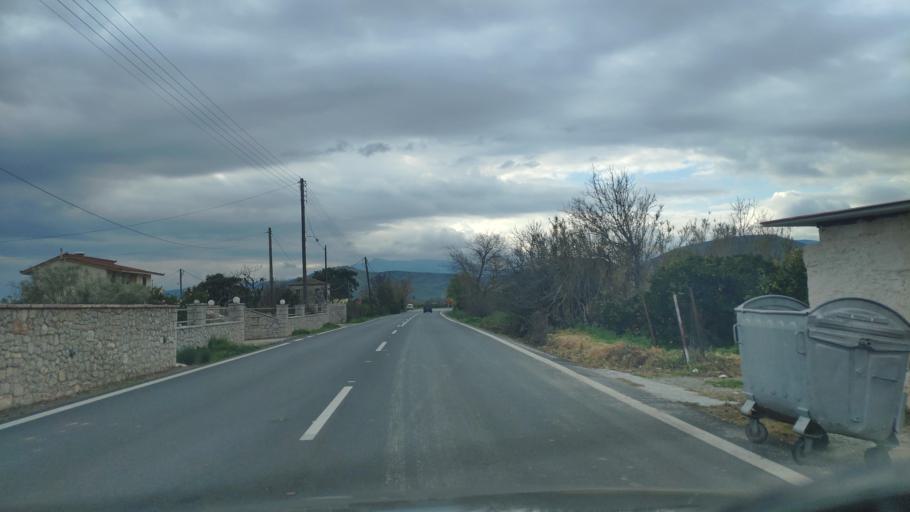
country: GR
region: Peloponnese
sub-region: Nomos Argolidos
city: Nea Kios
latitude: 37.5804
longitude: 22.7094
